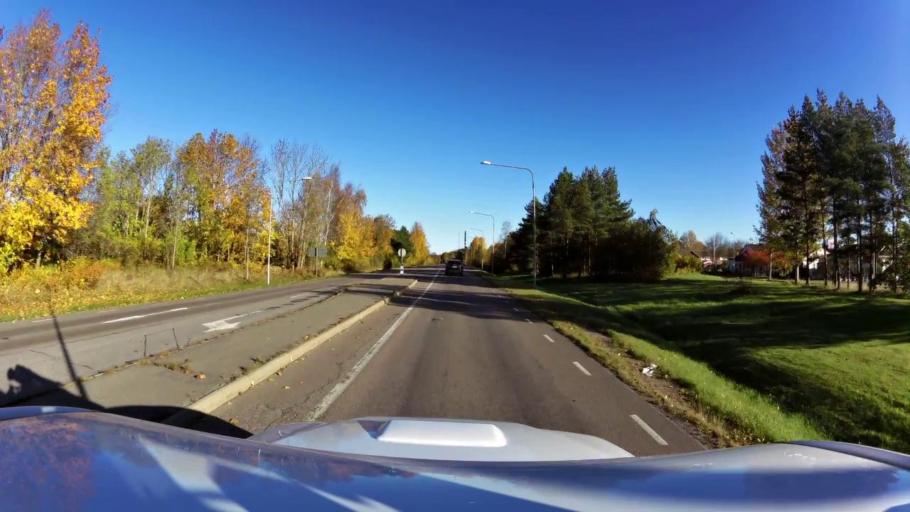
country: SE
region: OEstergoetland
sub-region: Linkopings Kommun
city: Ljungsbro
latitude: 58.4941
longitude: 15.5014
